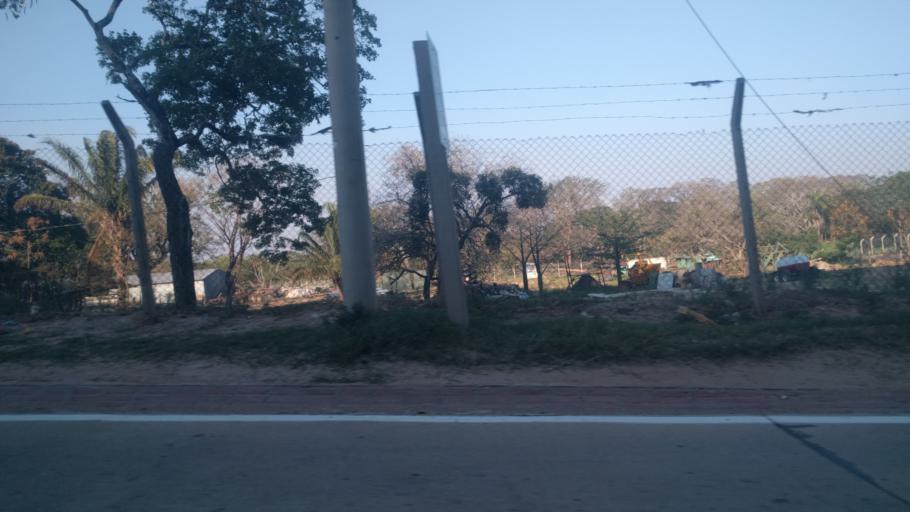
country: BO
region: Santa Cruz
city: Santa Cruz de la Sierra
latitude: -17.7511
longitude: -63.2162
